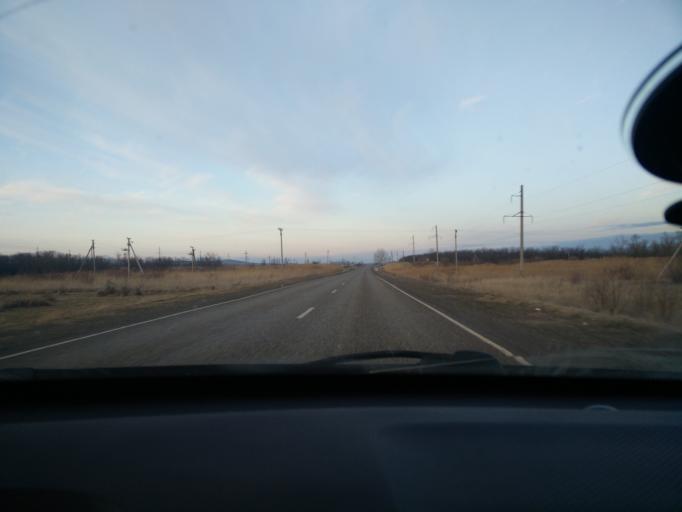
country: RU
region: Stavropol'skiy
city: Tatarka
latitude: 44.9970
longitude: 41.7541
